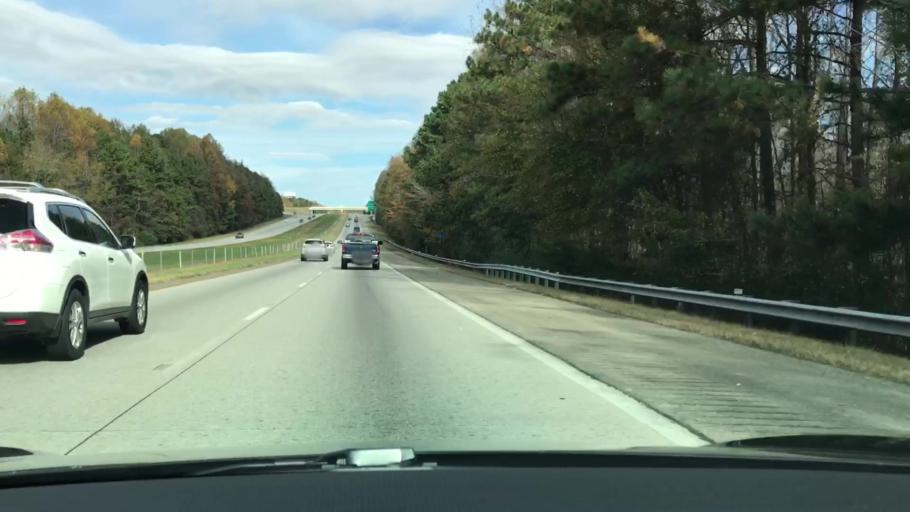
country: US
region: Georgia
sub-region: Gwinnett County
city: Buford
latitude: 34.1335
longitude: -83.9570
